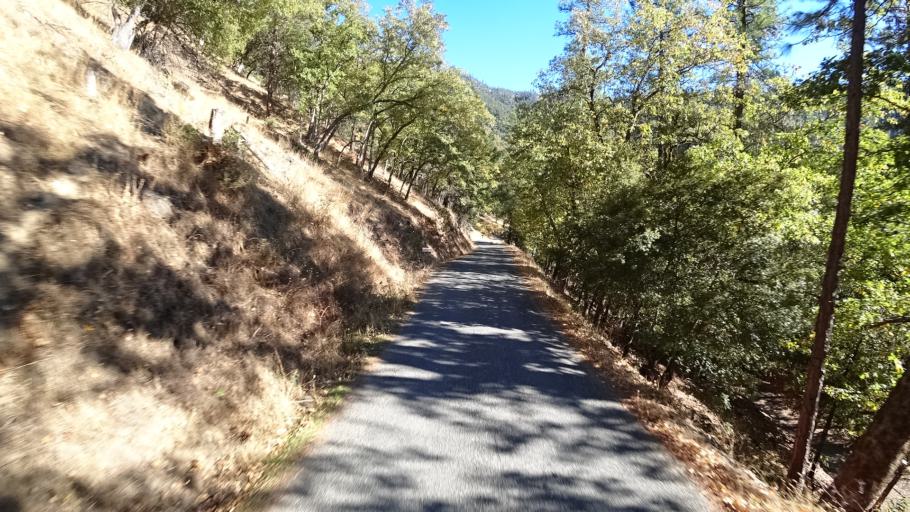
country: US
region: California
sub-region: Humboldt County
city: Willow Creek
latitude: 41.2839
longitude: -123.2620
